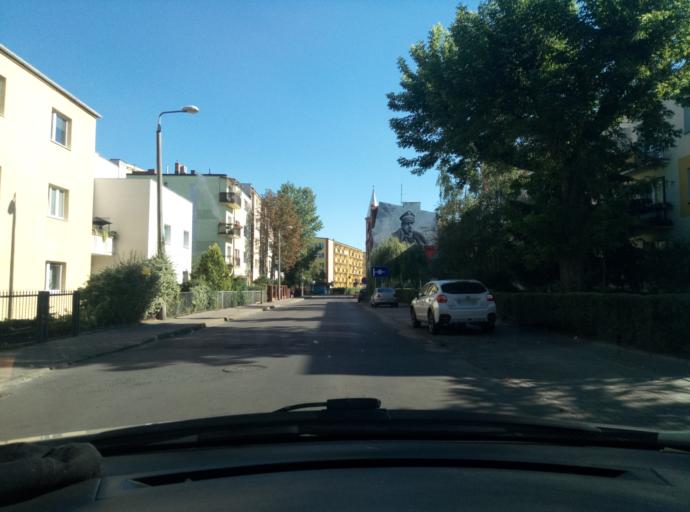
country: PL
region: Kujawsko-Pomorskie
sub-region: Torun
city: Torun
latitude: 53.0168
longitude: 18.5916
